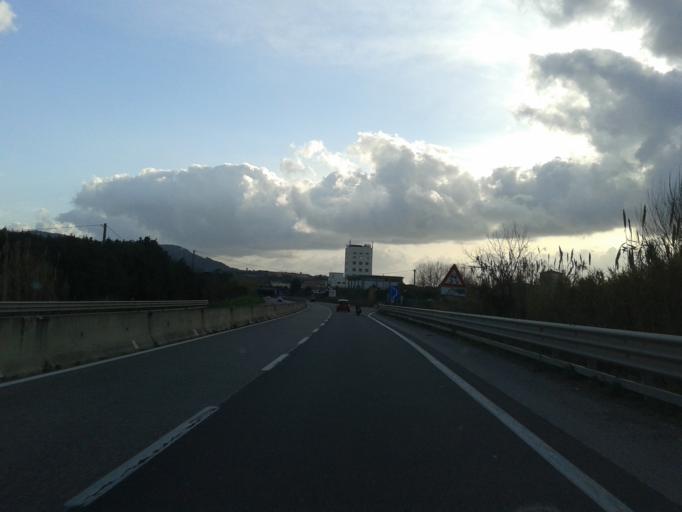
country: IT
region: Tuscany
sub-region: Provincia di Livorno
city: Livorno
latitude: 43.5239
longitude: 10.3312
